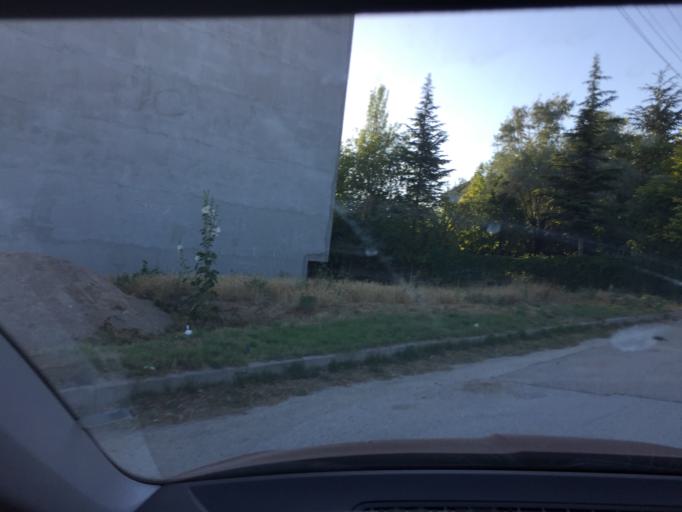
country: TR
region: Eskisehir
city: Eskisehir
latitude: 39.7748
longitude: 30.4531
